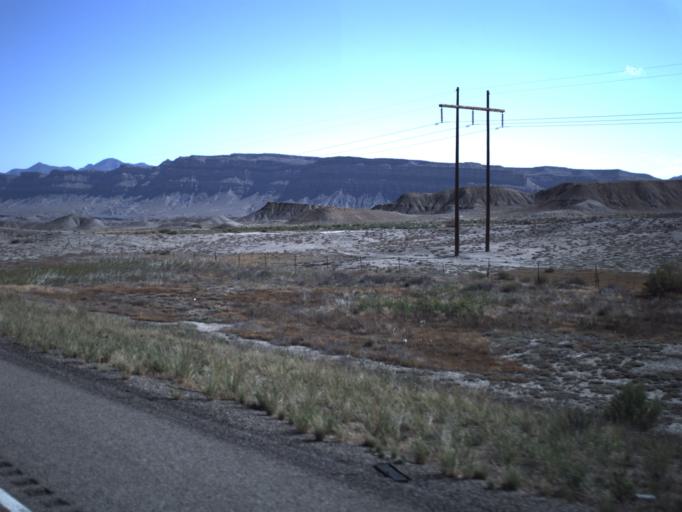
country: US
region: Utah
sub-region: Carbon County
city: East Carbon City
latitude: 39.2170
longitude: -110.3386
